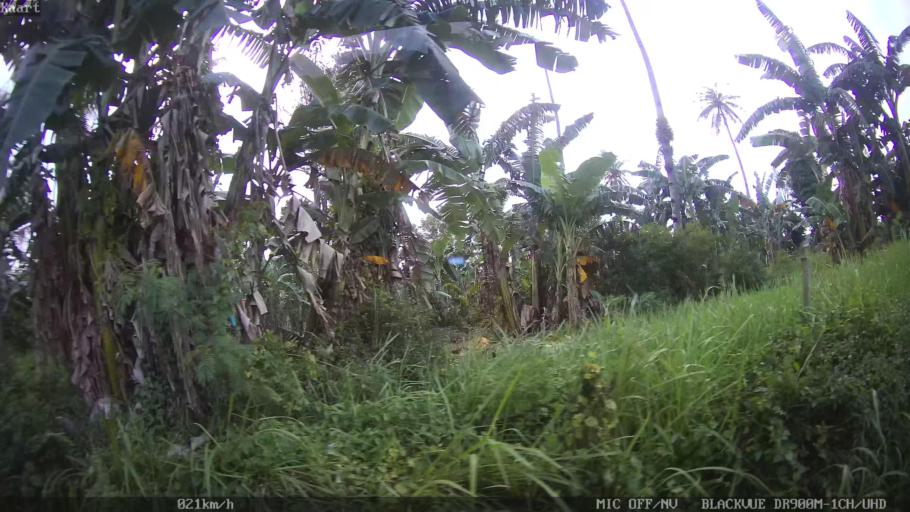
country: ID
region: Lampung
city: Kedaton
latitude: -5.3889
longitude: 105.2275
